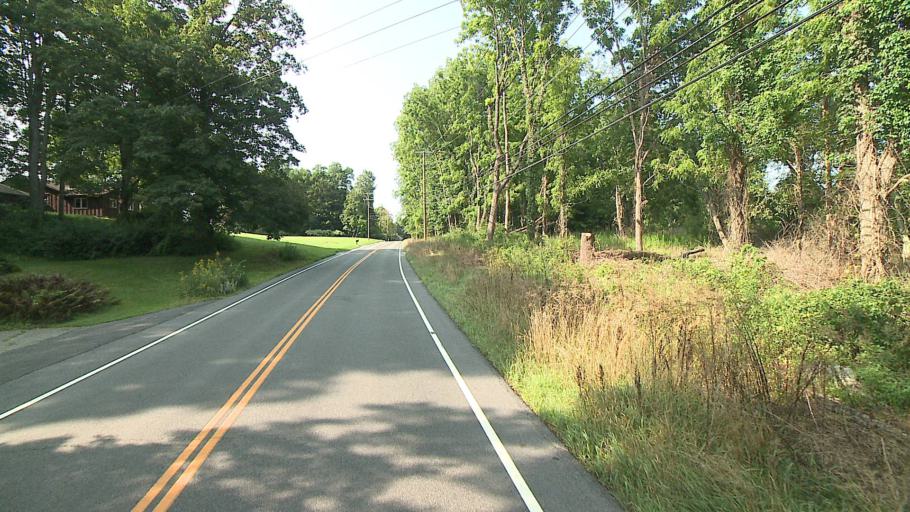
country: US
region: Connecticut
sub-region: Litchfield County
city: Kent
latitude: 41.7527
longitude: -73.4431
